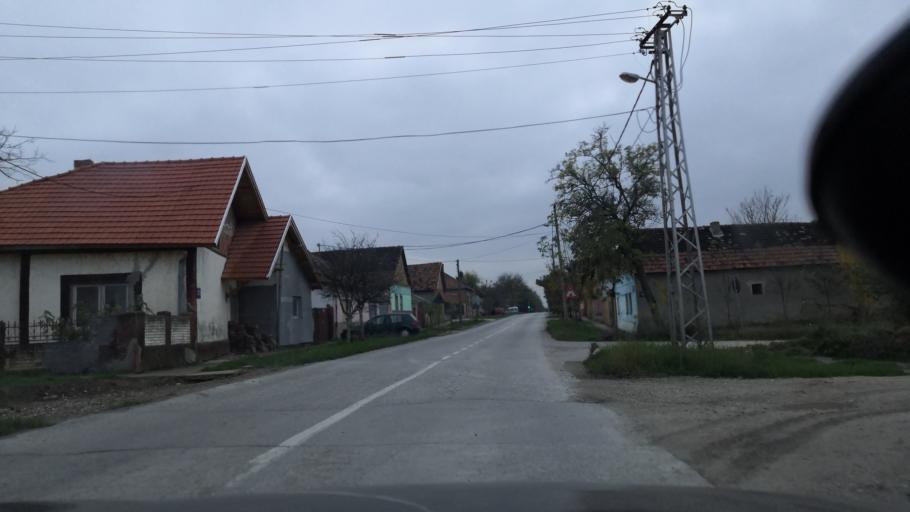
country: RS
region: Autonomna Pokrajina Vojvodina
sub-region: Severnobanatski Okrug
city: Novi Knezevac
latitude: 46.0453
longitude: 20.1032
